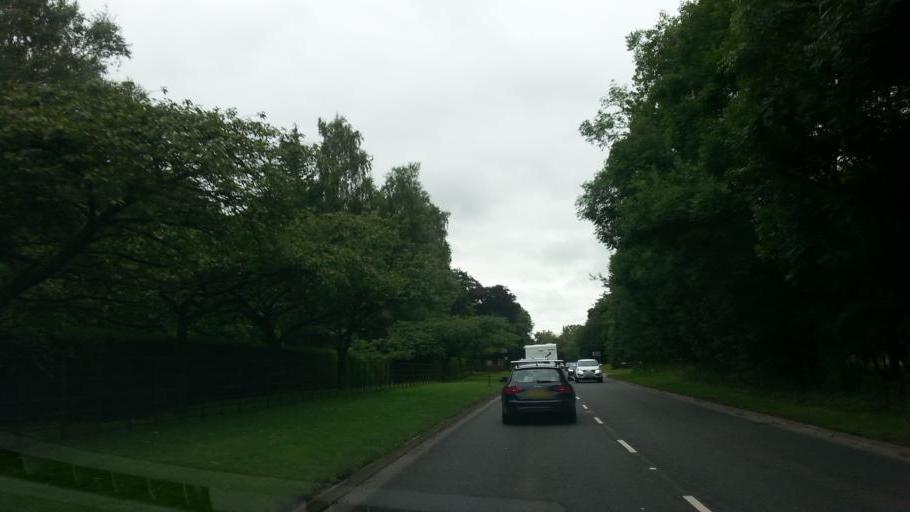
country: GB
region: England
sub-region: Wiltshire
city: Melksham
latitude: 51.3901
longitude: -2.1414
